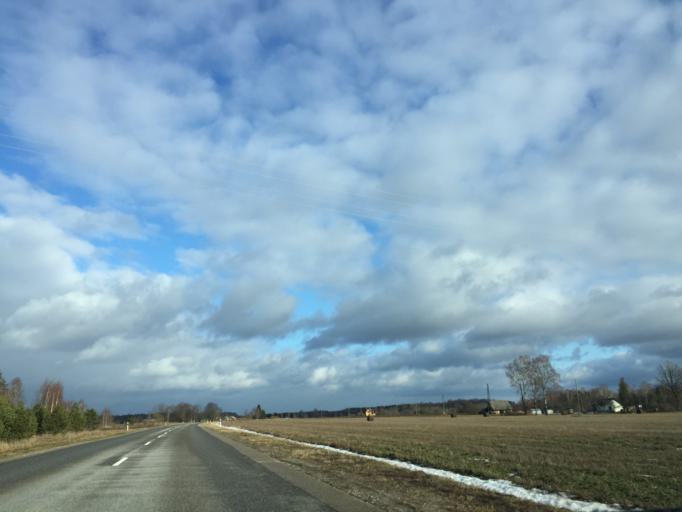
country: LV
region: Salacgrivas
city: Ainazi
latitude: 57.8627
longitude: 24.5426
